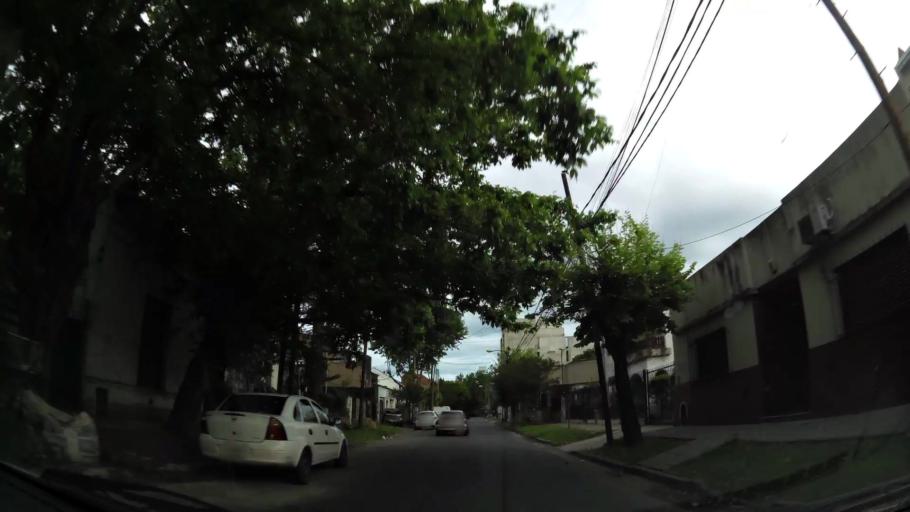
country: AR
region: Buenos Aires
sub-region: Partido de Quilmes
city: Quilmes
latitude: -34.7307
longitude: -58.2485
